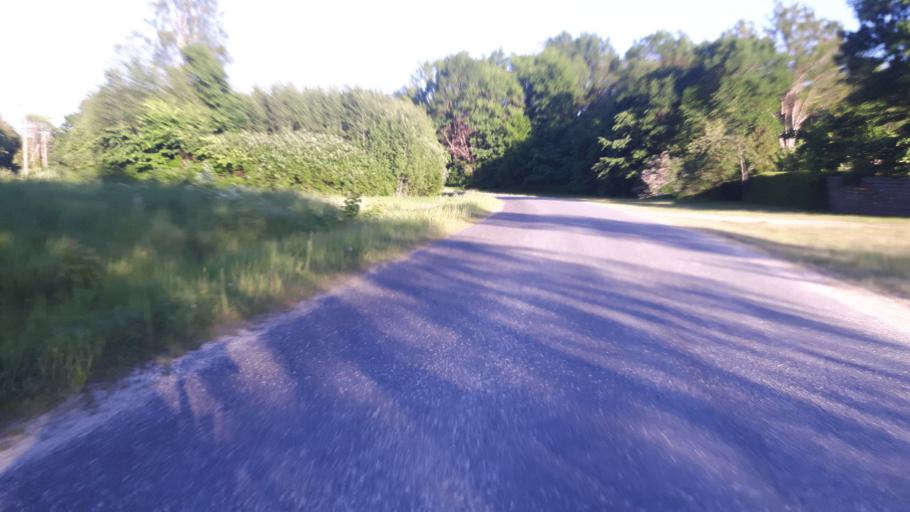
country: EE
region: Raplamaa
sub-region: Jaervakandi vald
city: Jarvakandi
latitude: 58.8123
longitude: 24.9167
